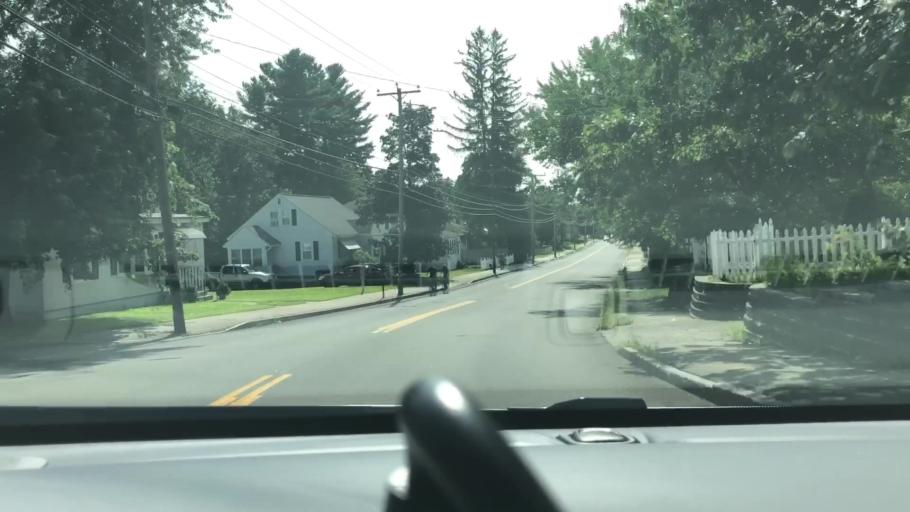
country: US
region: New Hampshire
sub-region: Hillsborough County
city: Pinardville
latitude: 42.9839
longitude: -71.4888
